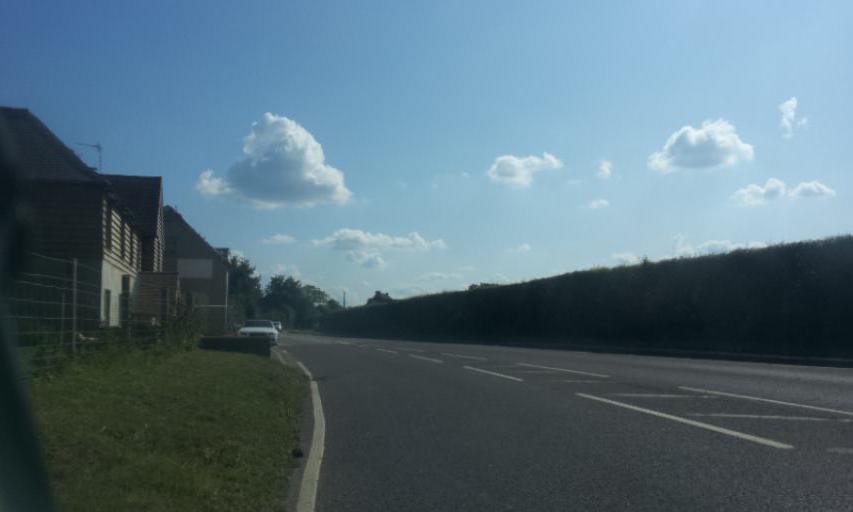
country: GB
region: England
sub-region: Kent
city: East Peckham
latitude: 51.2213
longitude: 0.3940
